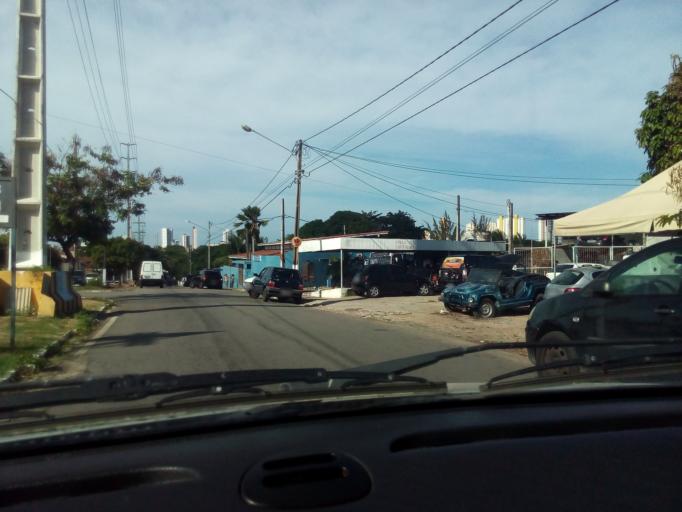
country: BR
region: Rio Grande do Norte
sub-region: Parnamirim
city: Parnamirim
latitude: -5.8707
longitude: -35.2081
